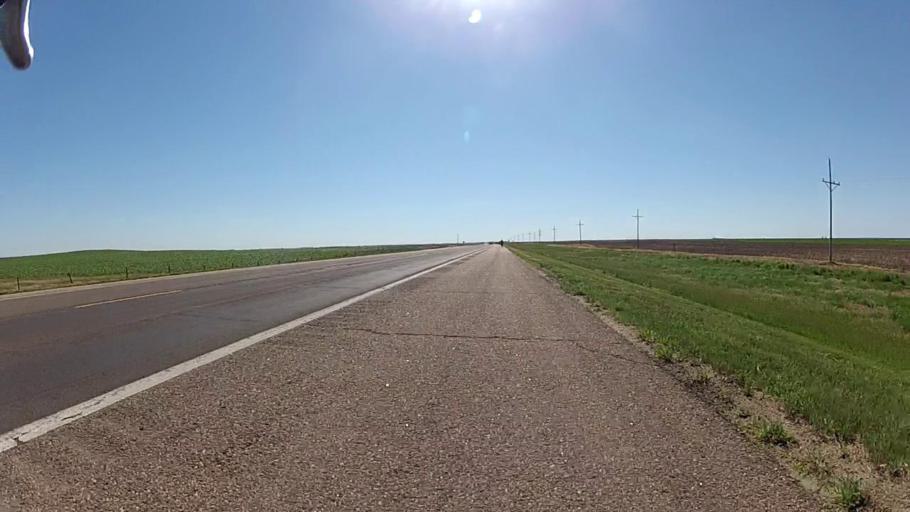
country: US
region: Kansas
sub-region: Kiowa County
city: Greensburg
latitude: 37.5863
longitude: -99.5548
